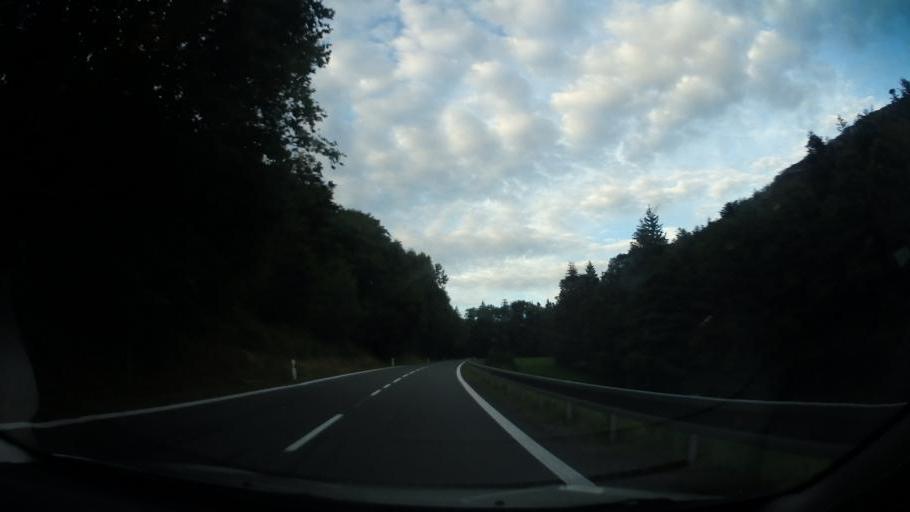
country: CZ
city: Rymarov
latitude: 49.8903
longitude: 17.2563
